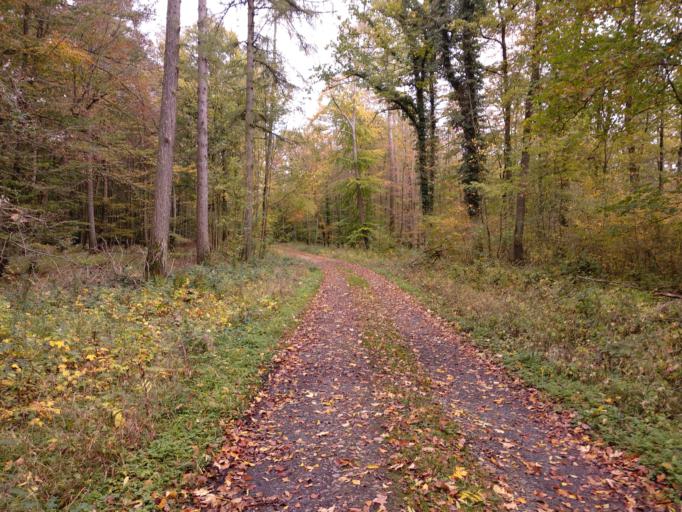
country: DE
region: North Rhine-Westphalia
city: Beverungen
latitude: 51.6636
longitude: 9.3321
